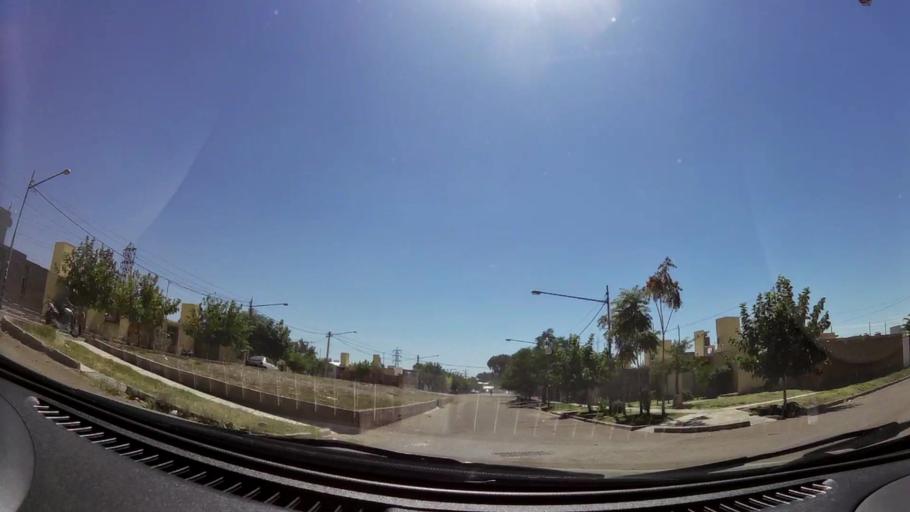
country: AR
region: Mendoza
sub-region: Departamento de Godoy Cruz
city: Godoy Cruz
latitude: -32.9312
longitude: -68.8680
